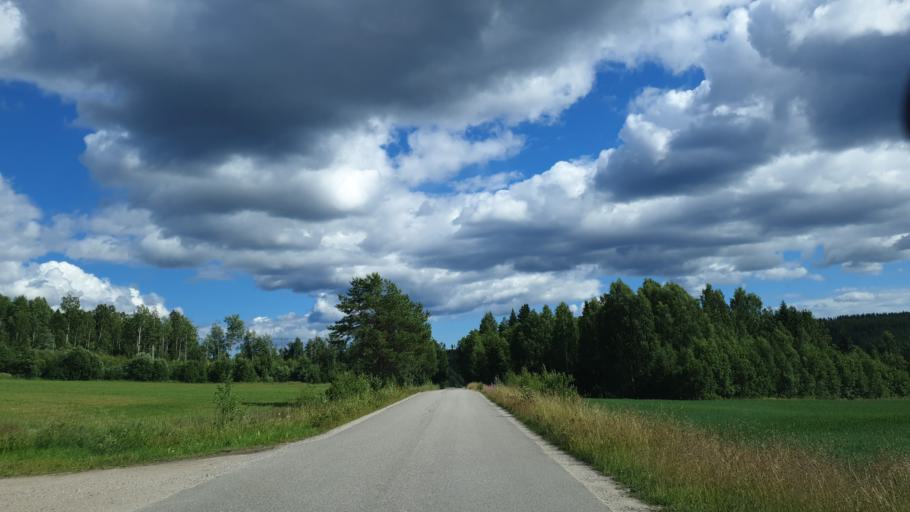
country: SE
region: Gaevleborg
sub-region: Nordanstigs Kommun
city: Bergsjoe
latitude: 62.0400
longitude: 17.0940
